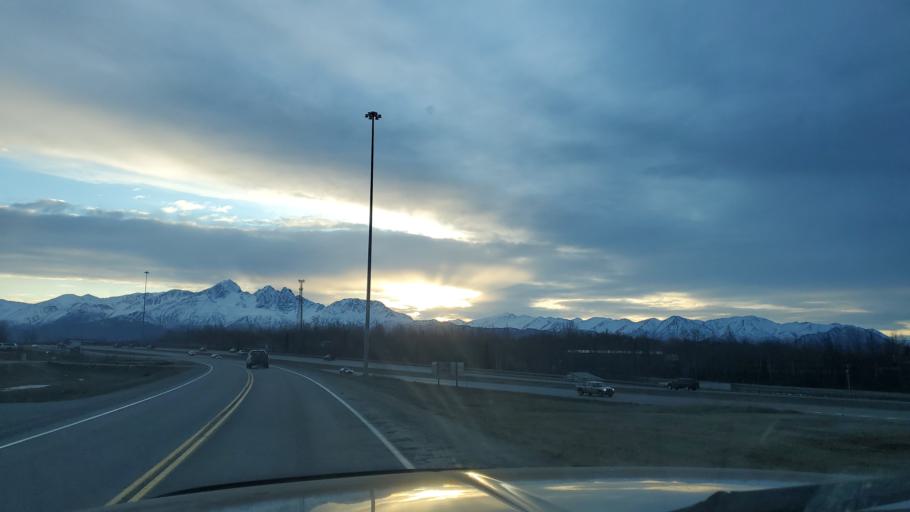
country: US
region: Alaska
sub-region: Matanuska-Susitna Borough
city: Lakes
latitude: 61.5667
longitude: -149.3080
